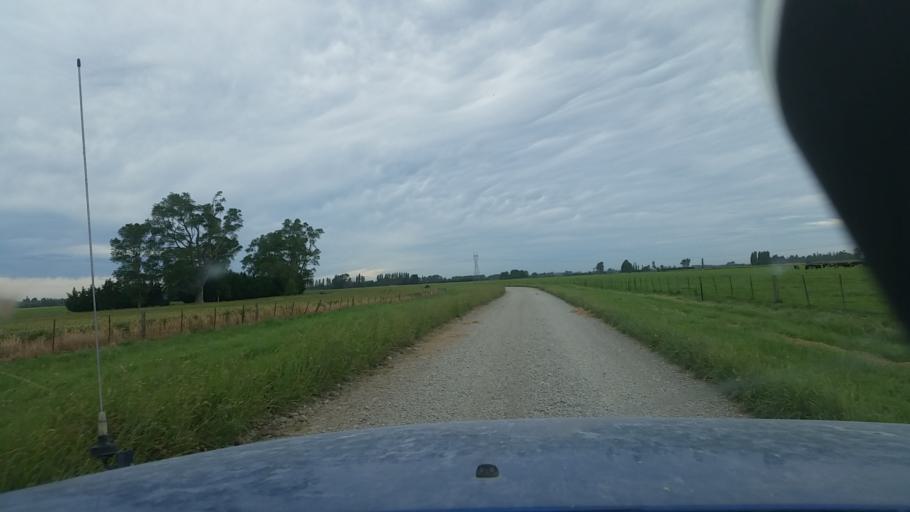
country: NZ
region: Canterbury
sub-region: Ashburton District
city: Ashburton
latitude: -43.8164
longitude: 171.6281
